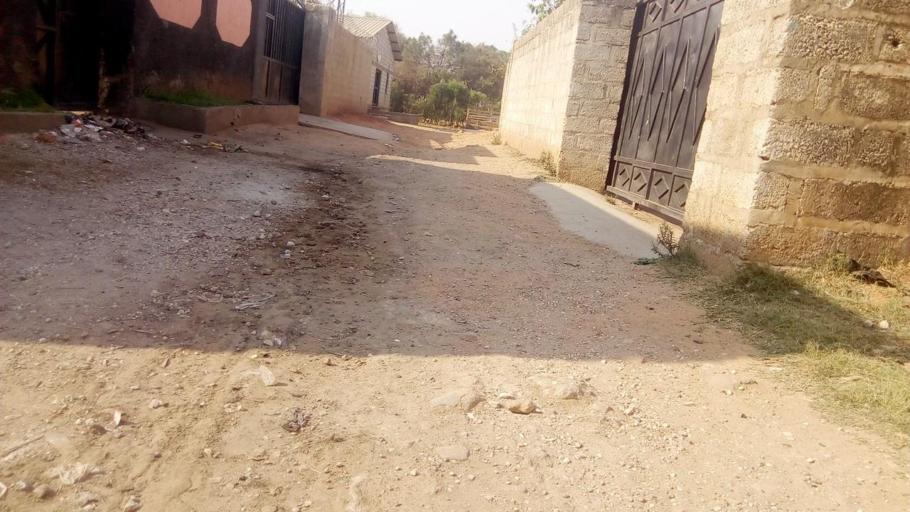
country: ZM
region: Lusaka
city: Lusaka
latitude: -15.3613
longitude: 28.2893
